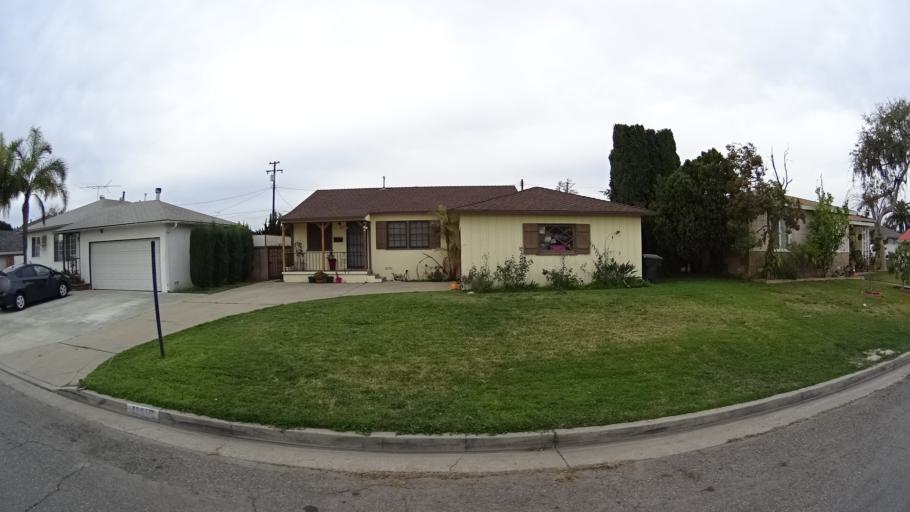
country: US
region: California
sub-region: Orange County
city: Garden Grove
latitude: 33.7799
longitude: -117.9296
